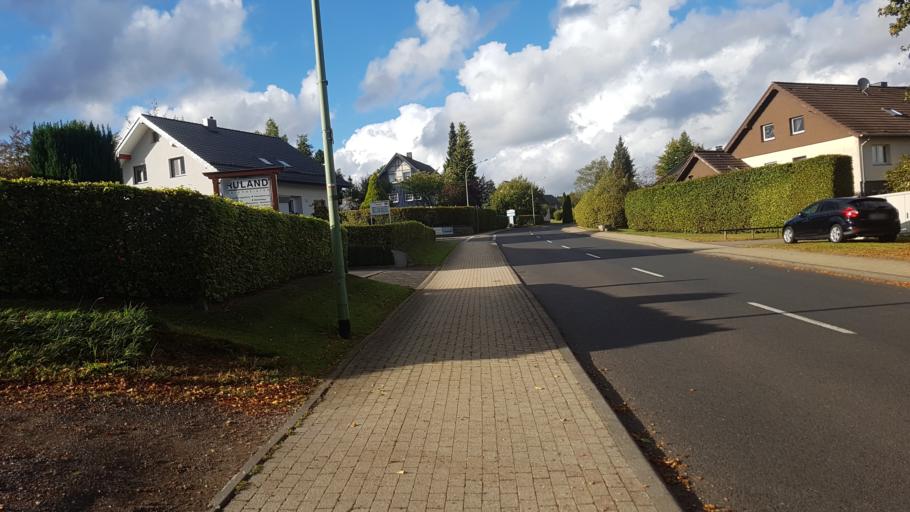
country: DE
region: North Rhine-Westphalia
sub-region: Regierungsbezirk Koln
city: Monschau
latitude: 50.5678
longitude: 6.2199
